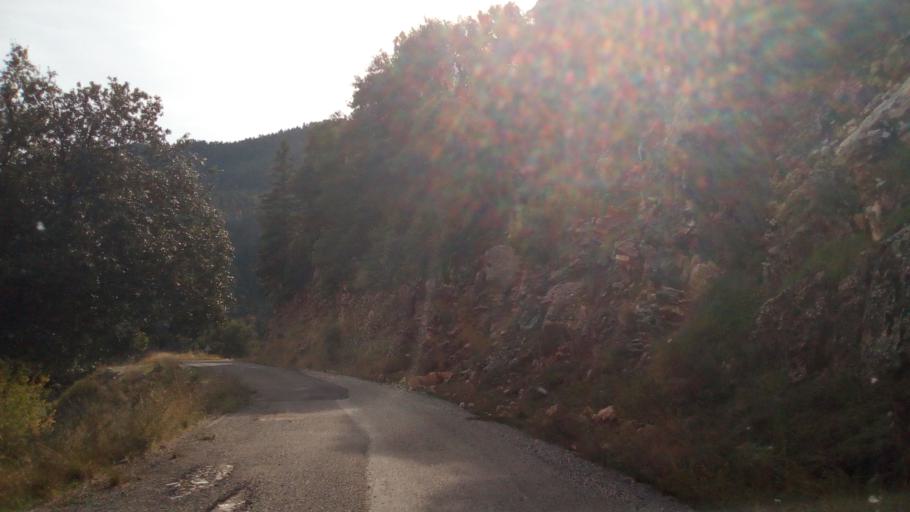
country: GR
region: West Greece
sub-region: Nomos Aitolias kai Akarnanias
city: Thermo
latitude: 38.5726
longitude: 21.8216
